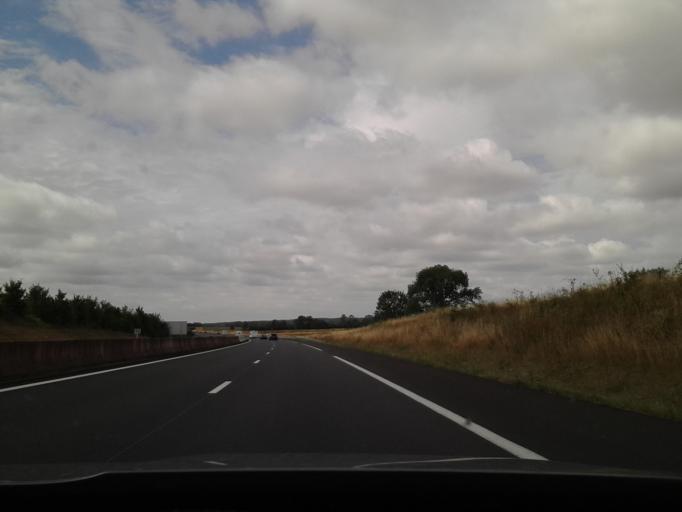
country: FR
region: Lower Normandy
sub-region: Departement de l'Orne
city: Sees
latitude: 48.5944
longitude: 0.1893
